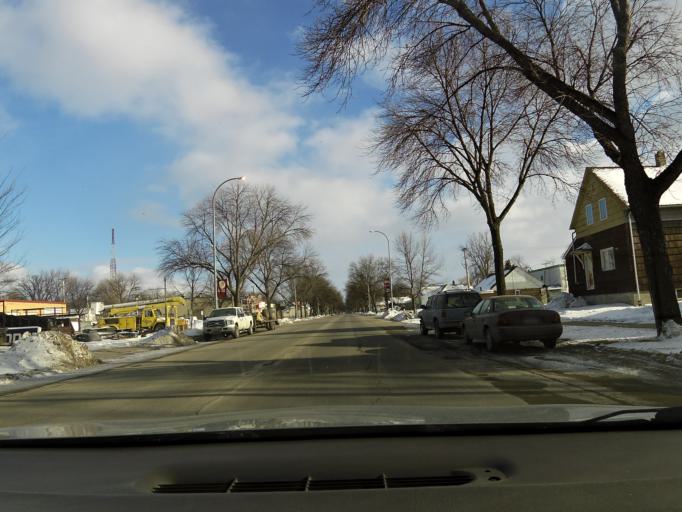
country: US
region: North Dakota
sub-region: Grand Forks County
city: Grand Forks
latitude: 47.9323
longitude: -97.0477
